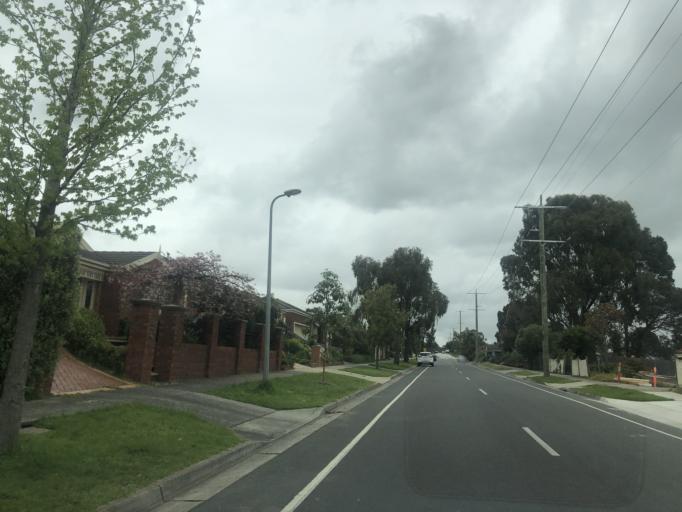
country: AU
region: Victoria
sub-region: Knox
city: Rowville
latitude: -37.9368
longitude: 145.2489
